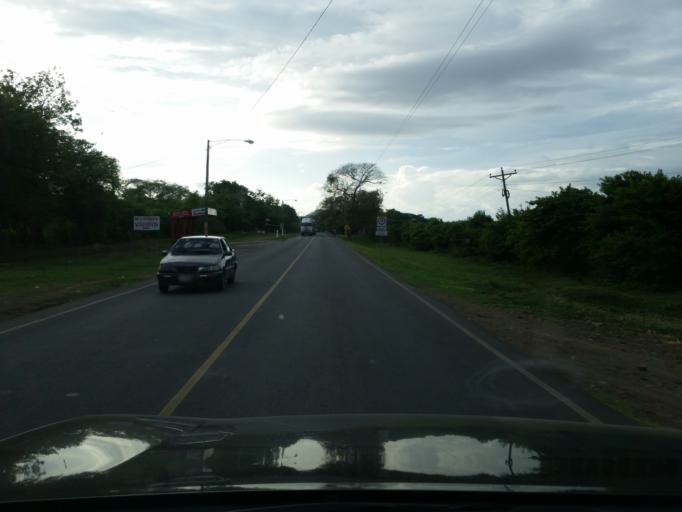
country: NI
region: Rivas
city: Belen
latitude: 11.5214
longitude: -85.8926
